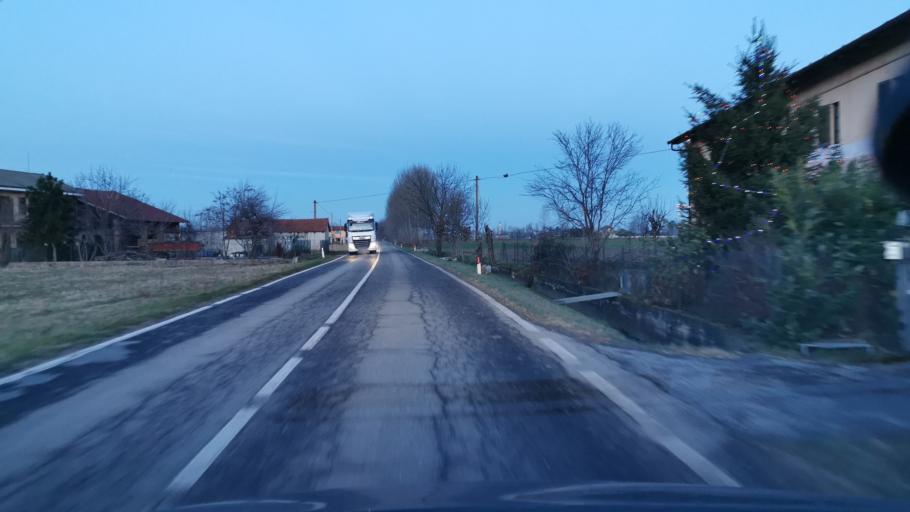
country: IT
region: Piedmont
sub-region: Provincia di Cuneo
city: Caraglio
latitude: 44.4469
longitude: 7.4728
